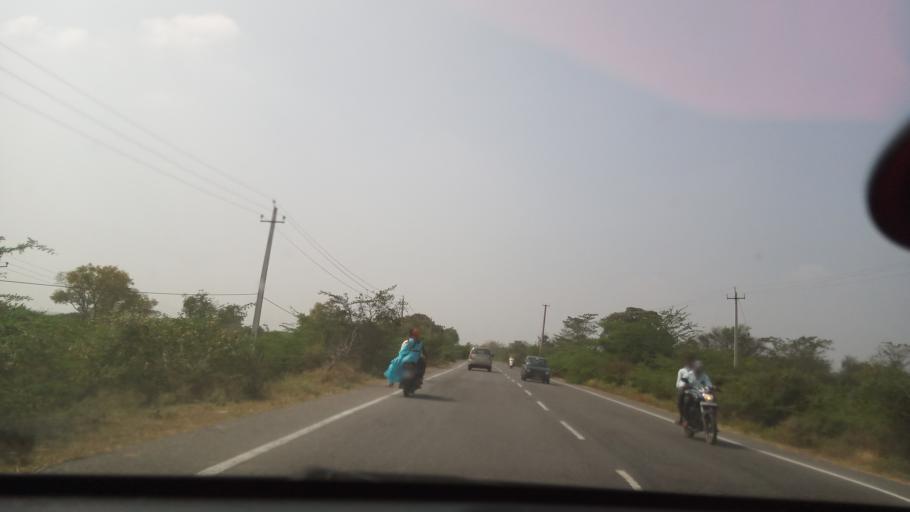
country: IN
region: Karnataka
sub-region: Mysore
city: Nanjangud
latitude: 12.0602
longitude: 76.7624
